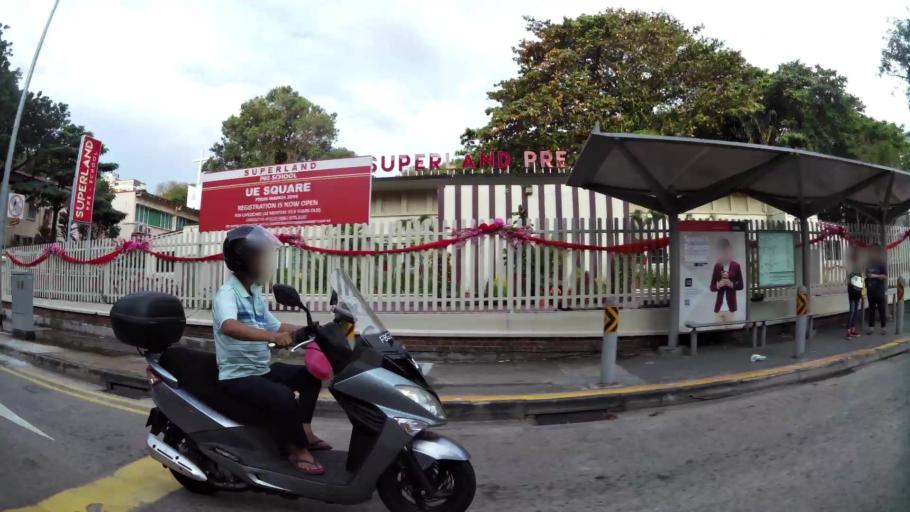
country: SG
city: Singapore
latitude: 1.2847
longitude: 103.8351
